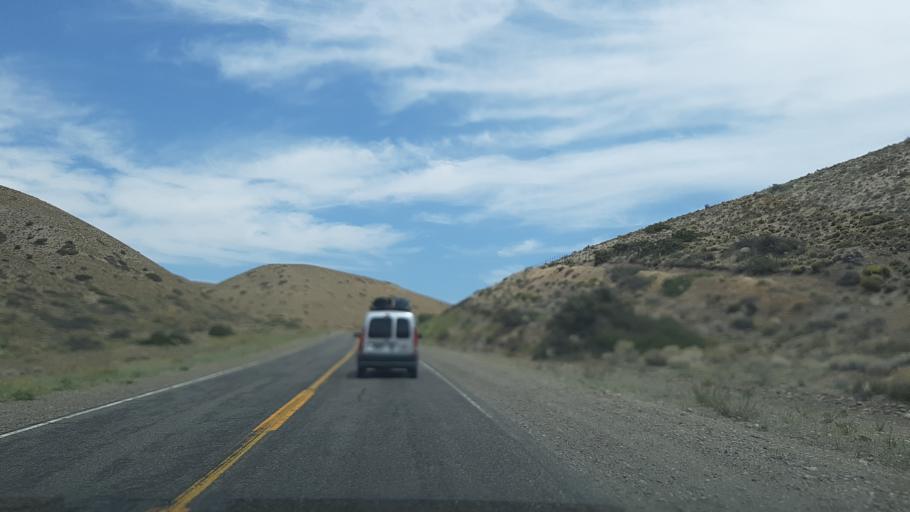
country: AR
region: Rio Negro
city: Pilcaniyeu
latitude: -40.4759
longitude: -70.6637
